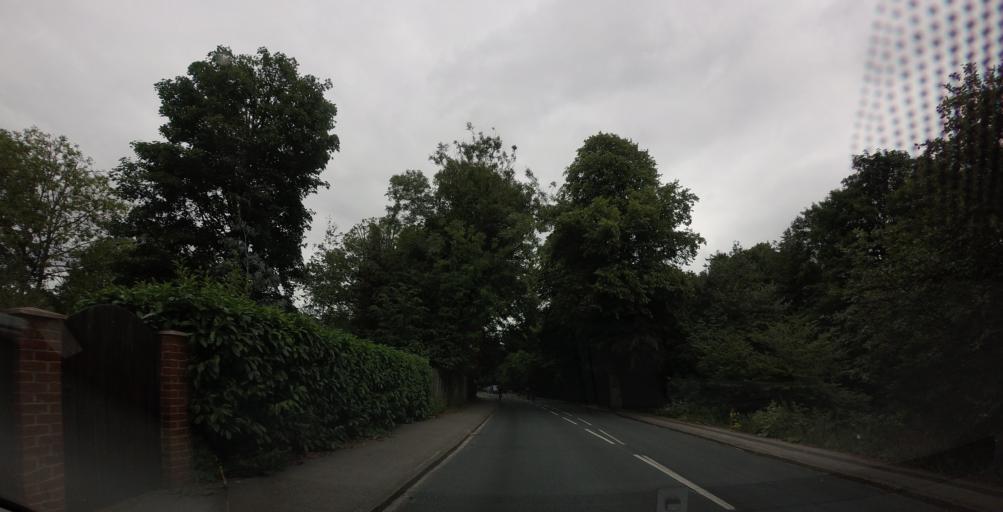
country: GB
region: England
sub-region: North Yorkshire
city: Ripon
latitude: 54.1335
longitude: -1.5373
